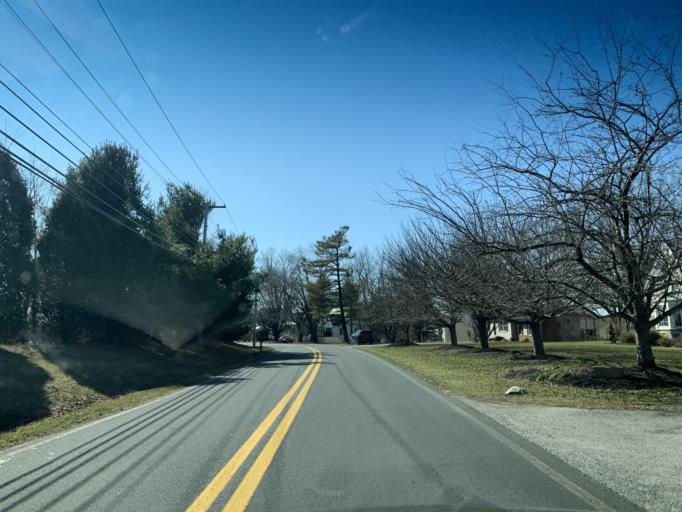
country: US
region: Maryland
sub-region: Carroll County
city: Hampstead
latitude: 39.5996
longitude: -76.8552
